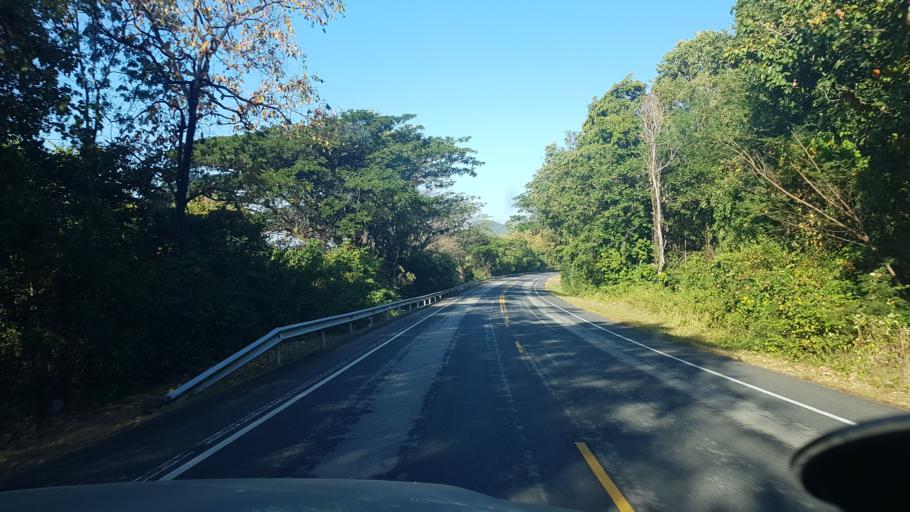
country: TH
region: Phetchabun
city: Lom Sak
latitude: 16.7394
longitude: 101.4146
